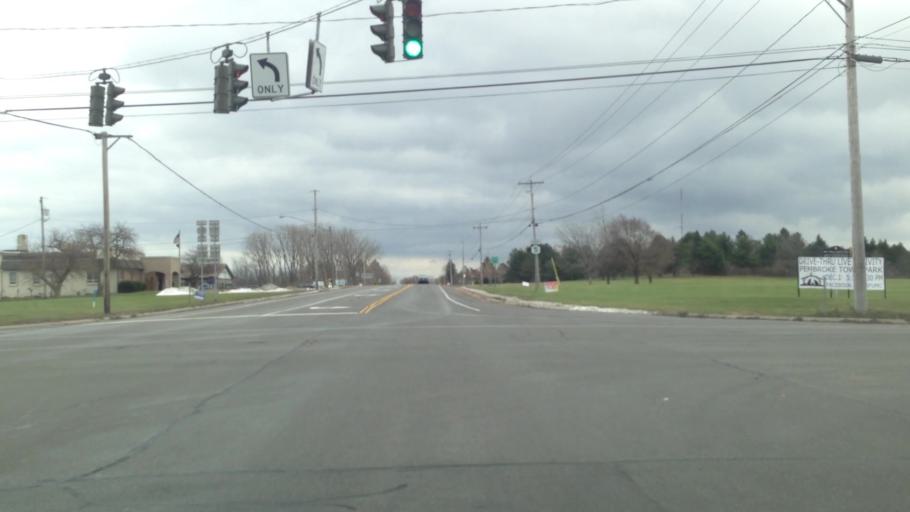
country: US
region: New York
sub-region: Erie County
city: Akron
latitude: 42.9930
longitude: -78.4062
